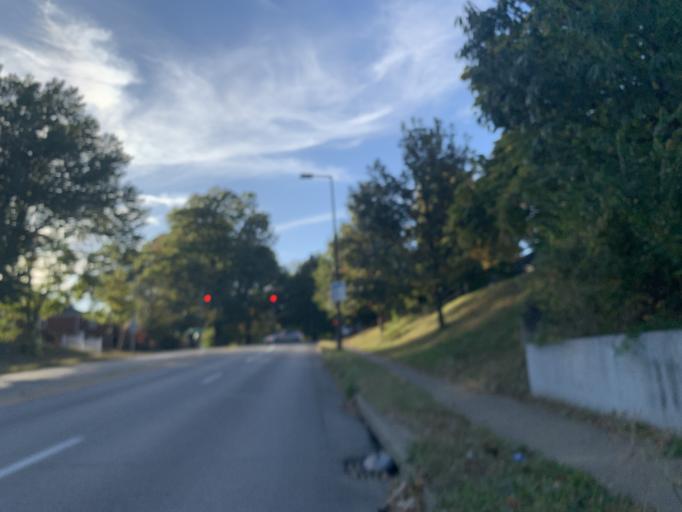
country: US
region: Kentucky
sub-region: Jefferson County
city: Louisville
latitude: 38.2220
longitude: -85.7821
